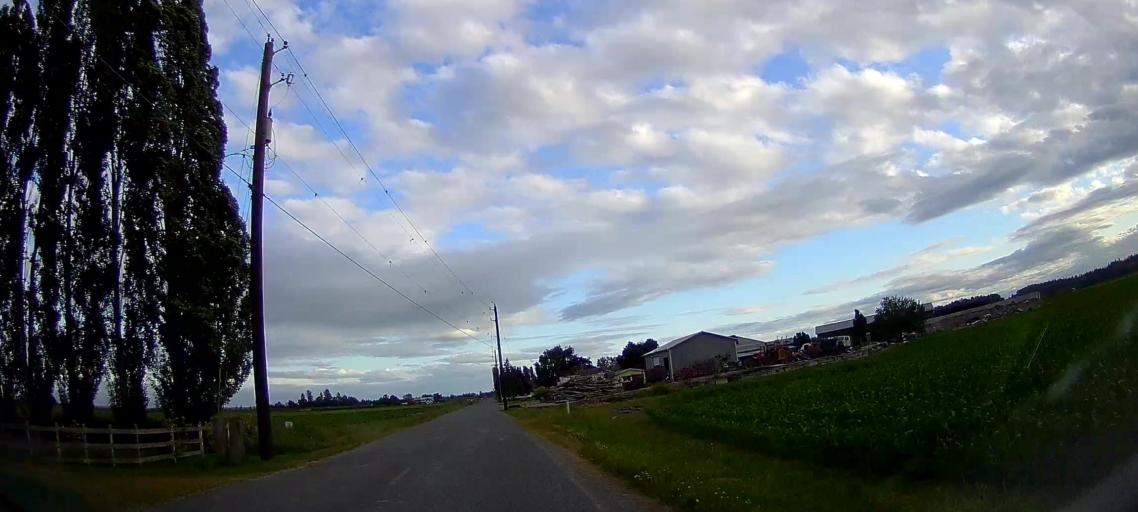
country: US
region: Washington
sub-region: Skagit County
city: Mount Vernon
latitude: 48.3763
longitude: -122.4007
